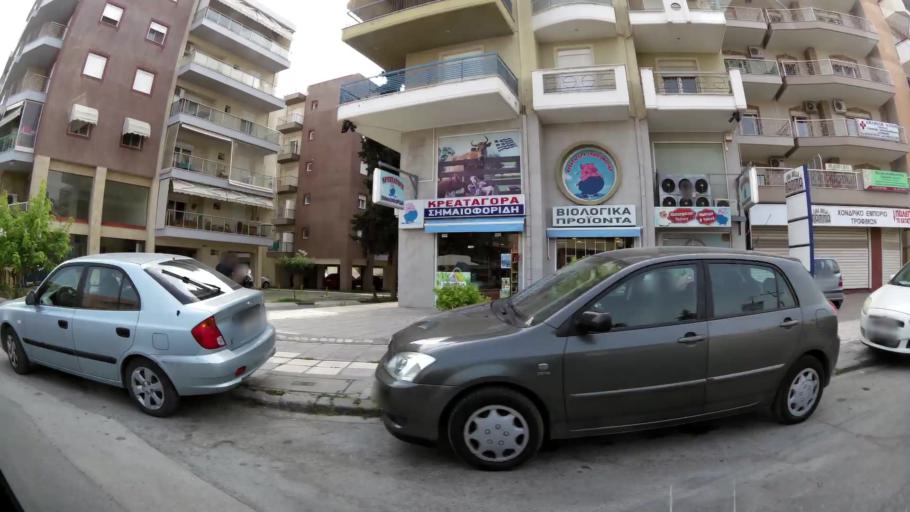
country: GR
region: Central Macedonia
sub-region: Nomos Thessalonikis
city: Stavroupoli
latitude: 40.6808
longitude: 22.9328
